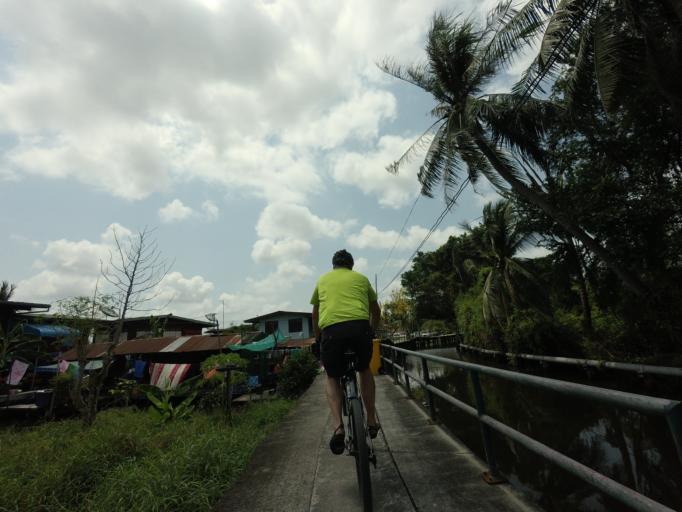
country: TH
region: Bangkok
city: Thung Khru
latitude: 13.6299
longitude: 100.4756
